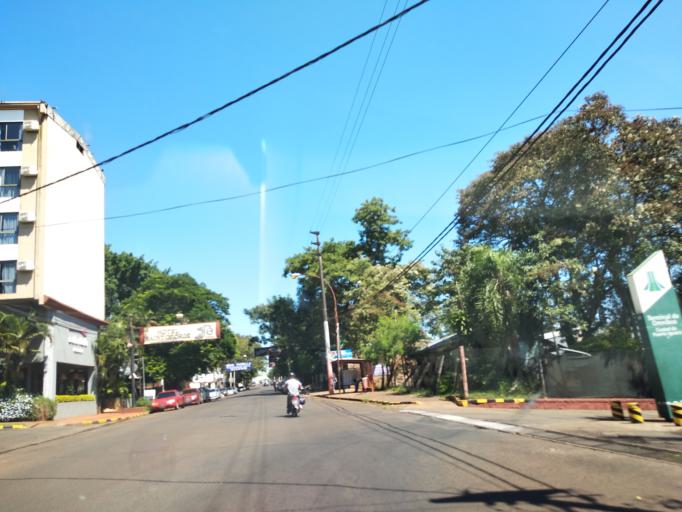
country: AR
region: Misiones
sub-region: Departamento de Iguazu
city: Puerto Iguazu
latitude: -25.5988
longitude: -54.5708
